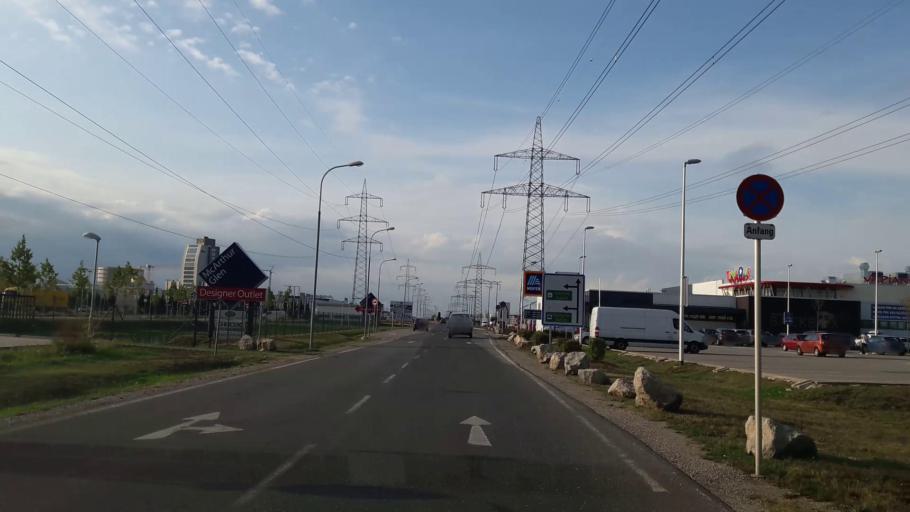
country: AT
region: Burgenland
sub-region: Politischer Bezirk Neusiedl am See
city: Parndorf
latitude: 47.9772
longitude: 16.8535
